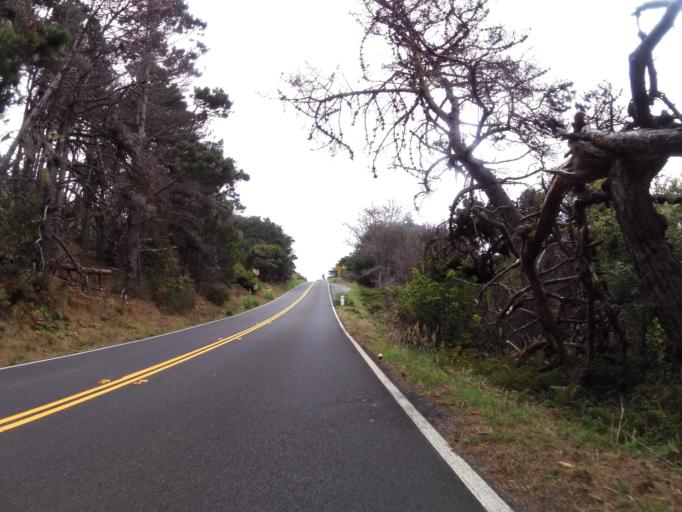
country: US
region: California
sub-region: Sonoma County
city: Sea Ranch
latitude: 38.5360
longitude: -123.2780
